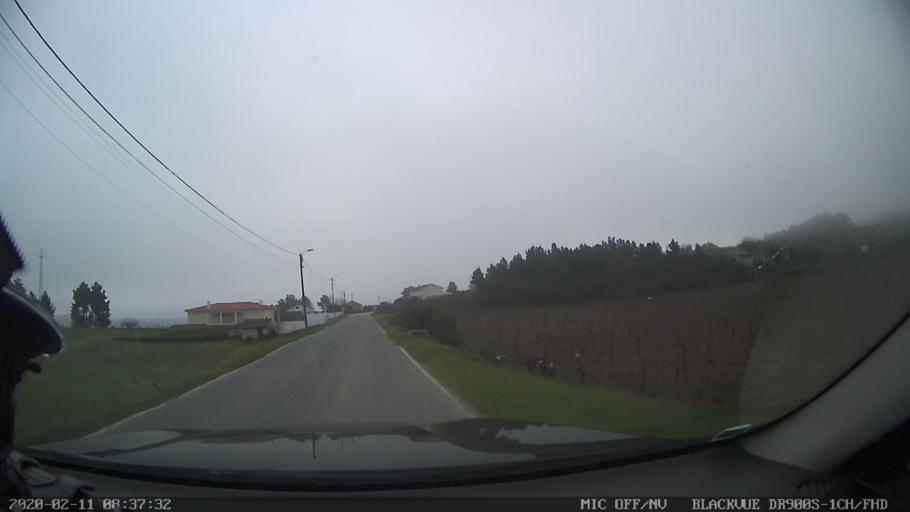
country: PT
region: Vila Real
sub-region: Sabrosa
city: Sabrosa
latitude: 41.2568
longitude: -7.5884
